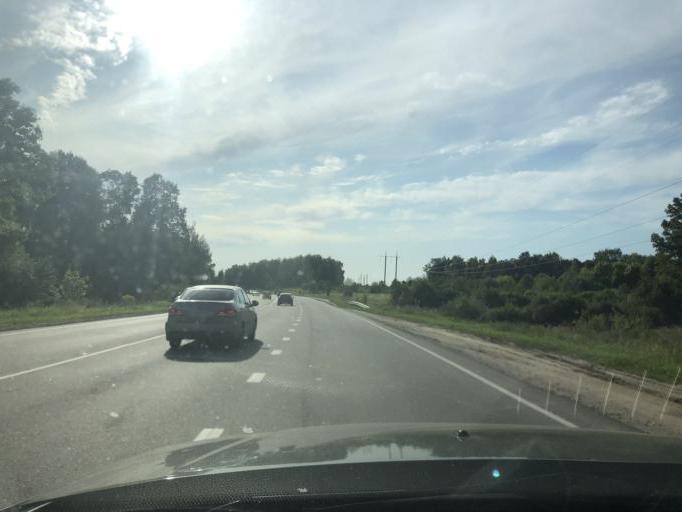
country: RU
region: Tula
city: Kosaya Gora
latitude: 54.1520
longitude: 37.4179
